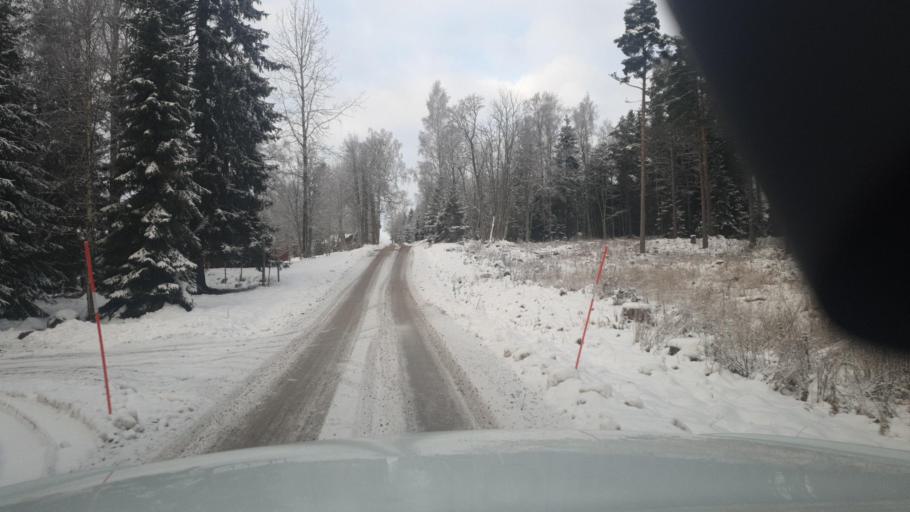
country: SE
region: Vaermland
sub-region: Torsby Kommun
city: Torsby
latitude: 59.9439
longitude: 12.7991
